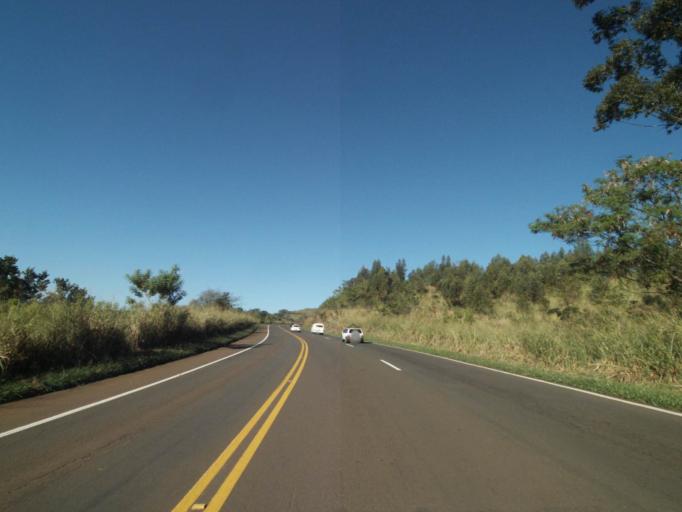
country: BR
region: Parana
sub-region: Londrina
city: Londrina
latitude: -23.6404
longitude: -51.1028
